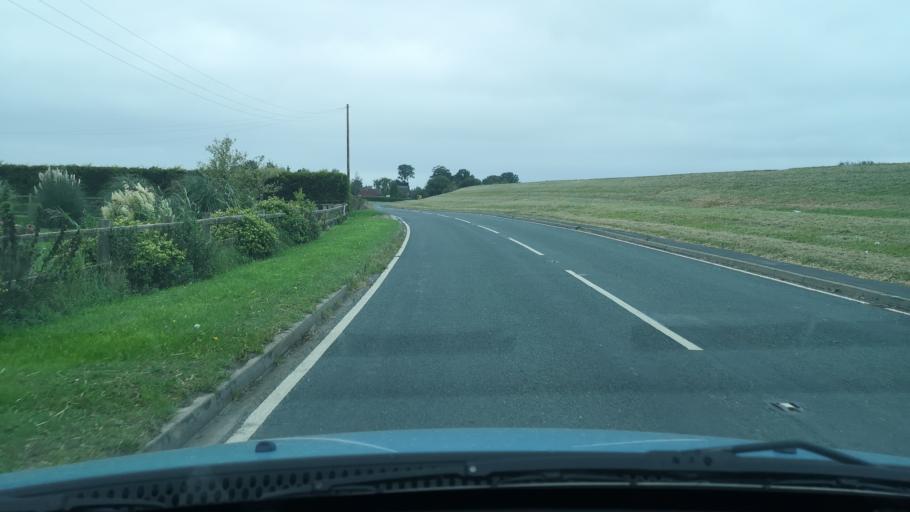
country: GB
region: England
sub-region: East Riding of Yorkshire
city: Goole
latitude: 53.6831
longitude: -0.8544
